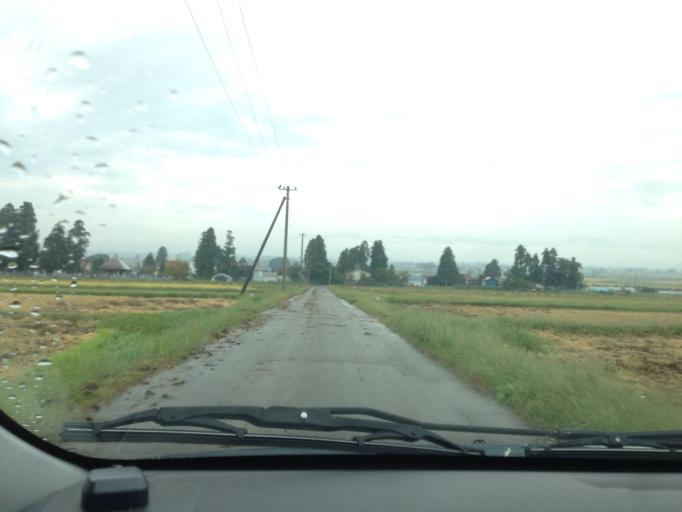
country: JP
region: Fukushima
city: Kitakata
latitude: 37.4940
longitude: 139.8180
